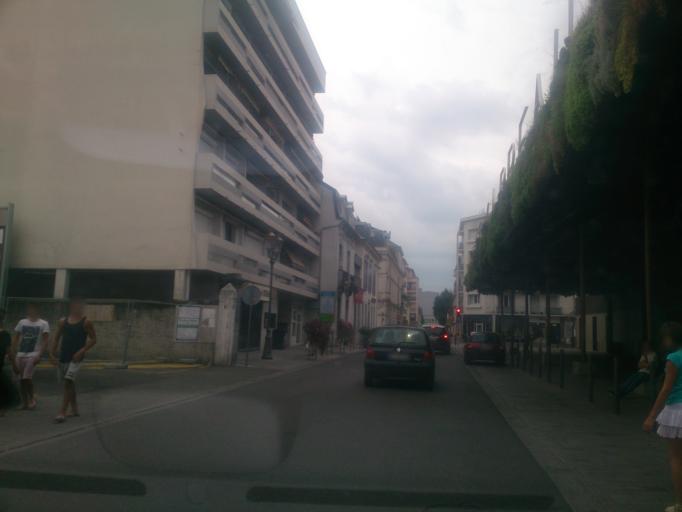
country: FR
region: Midi-Pyrenees
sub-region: Departement des Hautes-Pyrenees
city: Tarbes
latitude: 43.2310
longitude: 0.0757
